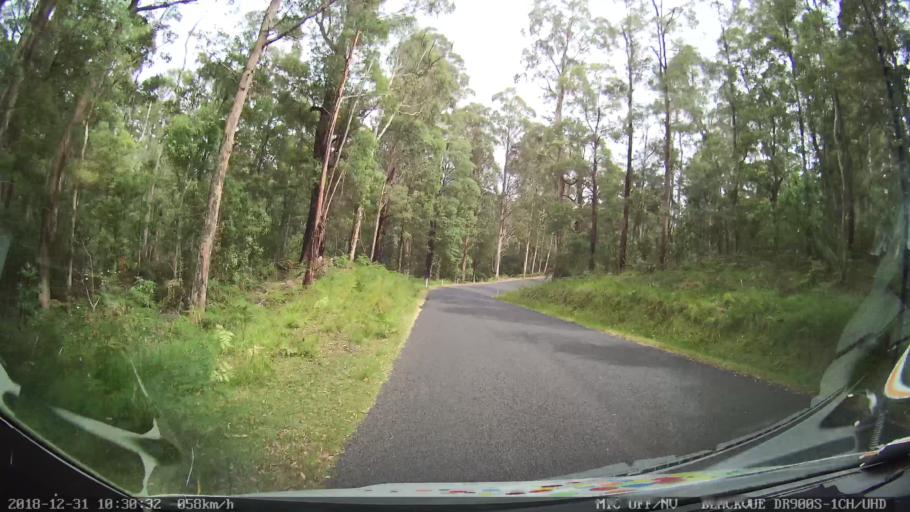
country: AU
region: New South Wales
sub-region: Snowy River
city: Jindabyne
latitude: -36.4623
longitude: 148.1511
